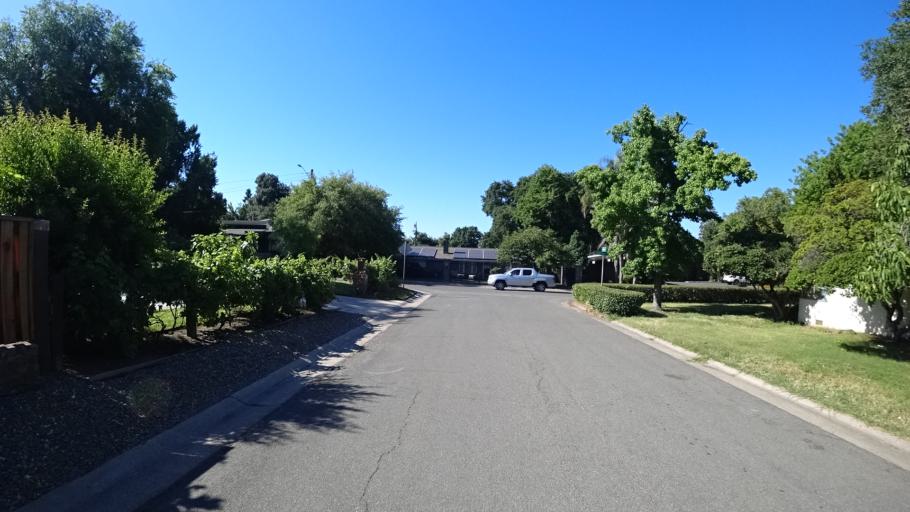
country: US
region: California
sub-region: Sacramento County
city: Sacramento
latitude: 38.5304
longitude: -121.5012
